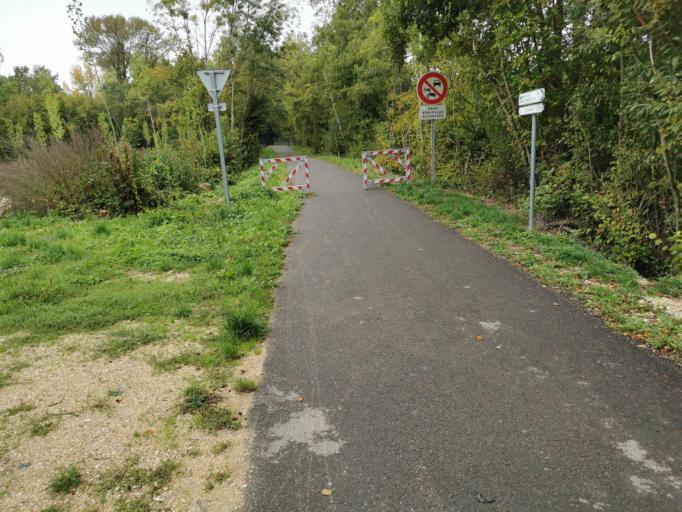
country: FR
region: Champagne-Ardenne
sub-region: Departement de l'Aube
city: Romilly-sur-Seine
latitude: 48.5529
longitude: 3.7043
